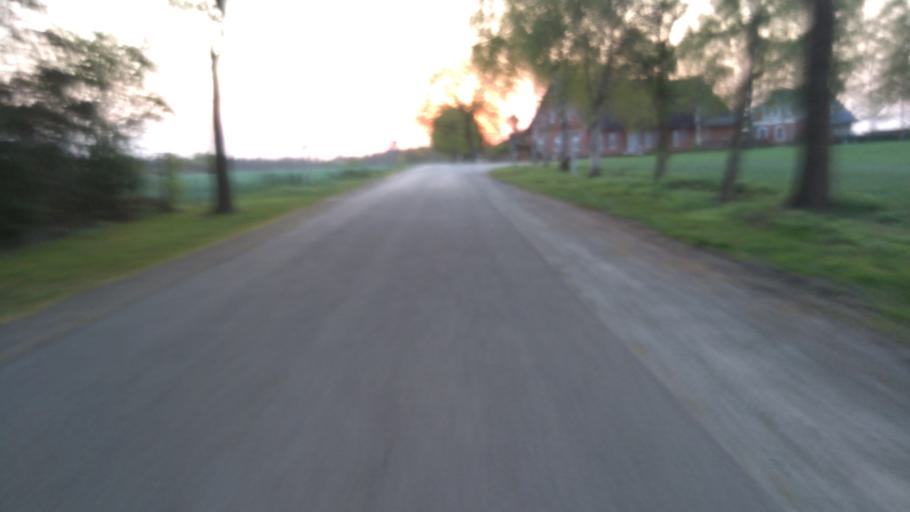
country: DE
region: Lower Saxony
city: Bargstedt
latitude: 53.4695
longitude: 9.4724
